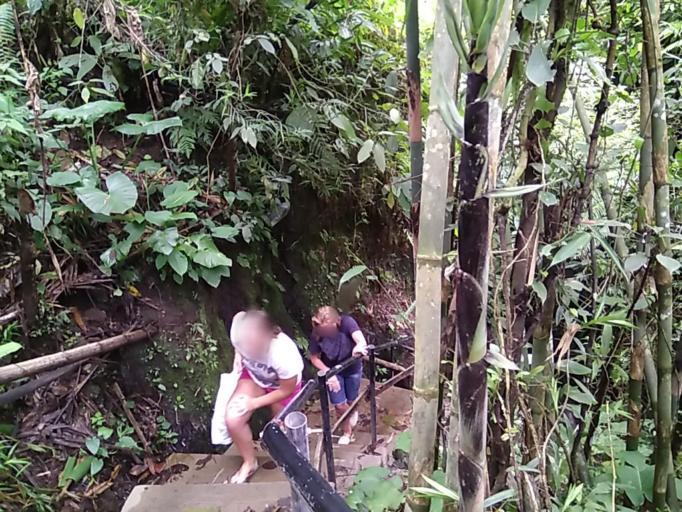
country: ID
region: Bali
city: Banjar Kubu
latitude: -8.4429
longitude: 115.3873
